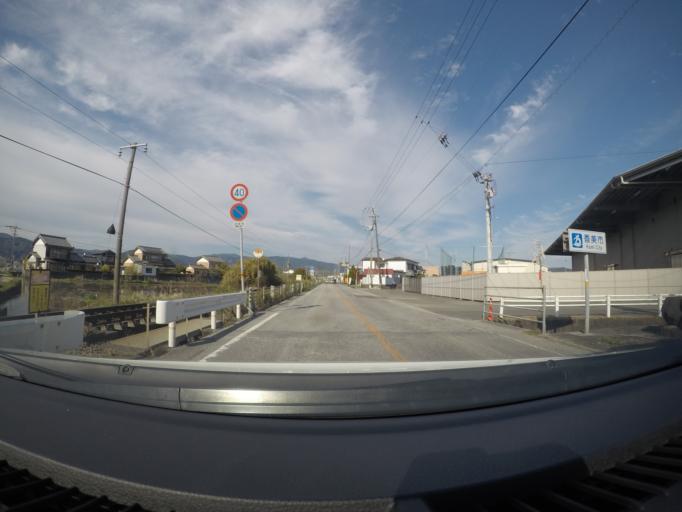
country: JP
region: Kochi
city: Kochi-shi
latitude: 33.5989
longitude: 133.6707
